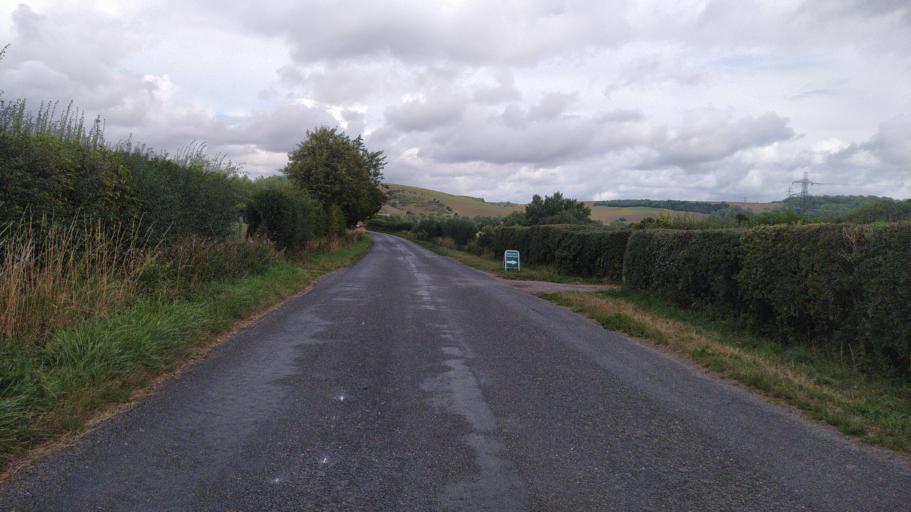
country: GB
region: England
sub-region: Hampshire
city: Cowplain
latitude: 50.9856
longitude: -1.0255
